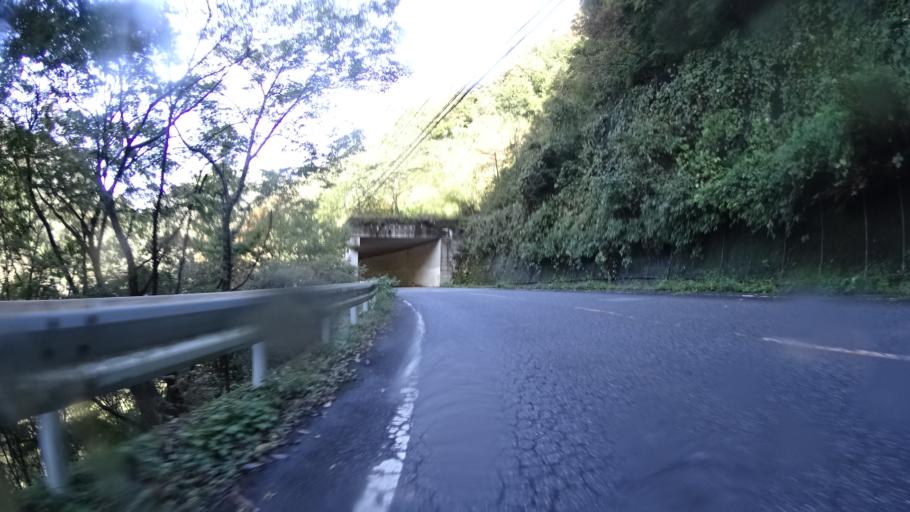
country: JP
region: Yamanashi
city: Otsuki
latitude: 35.7847
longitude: 138.9702
